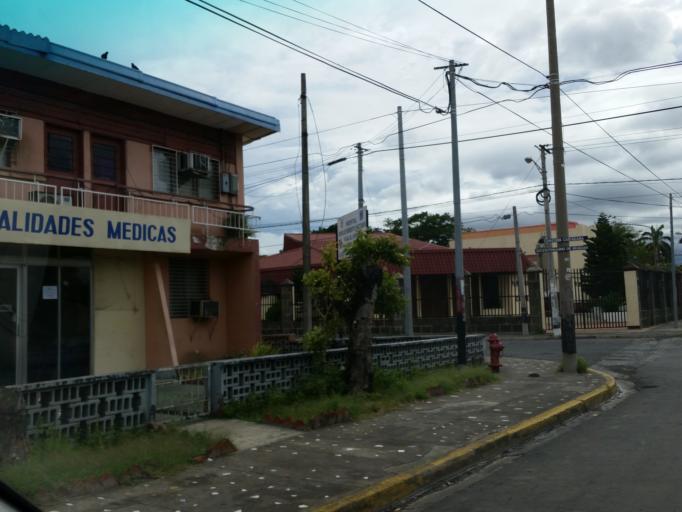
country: NI
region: Managua
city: Managua
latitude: 12.1472
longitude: -86.2839
